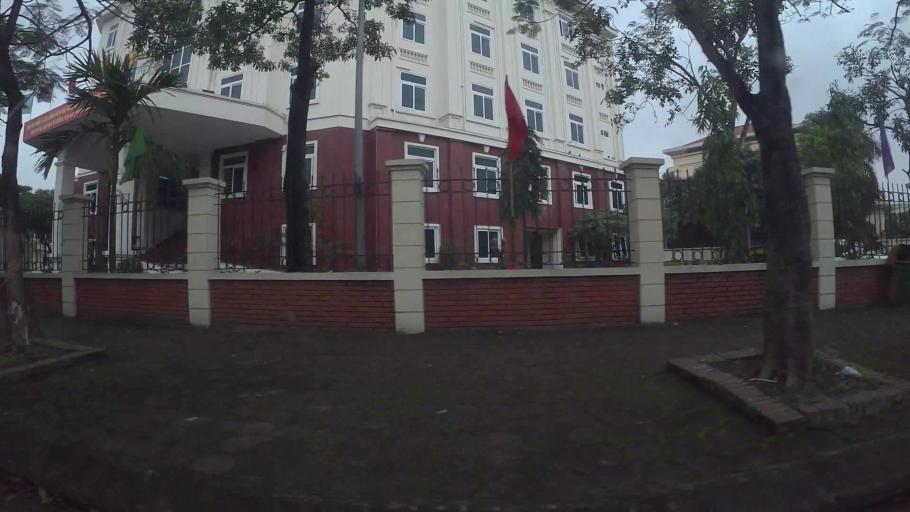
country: VN
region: Ha Noi
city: Van Dien
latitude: 20.9672
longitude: 105.8470
